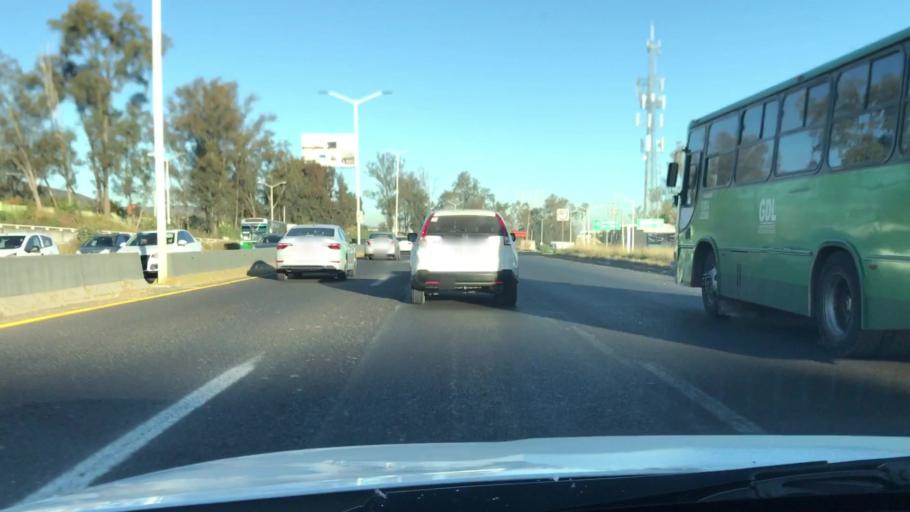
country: MX
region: Jalisco
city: Guadalajara
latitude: 20.6712
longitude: -103.4537
